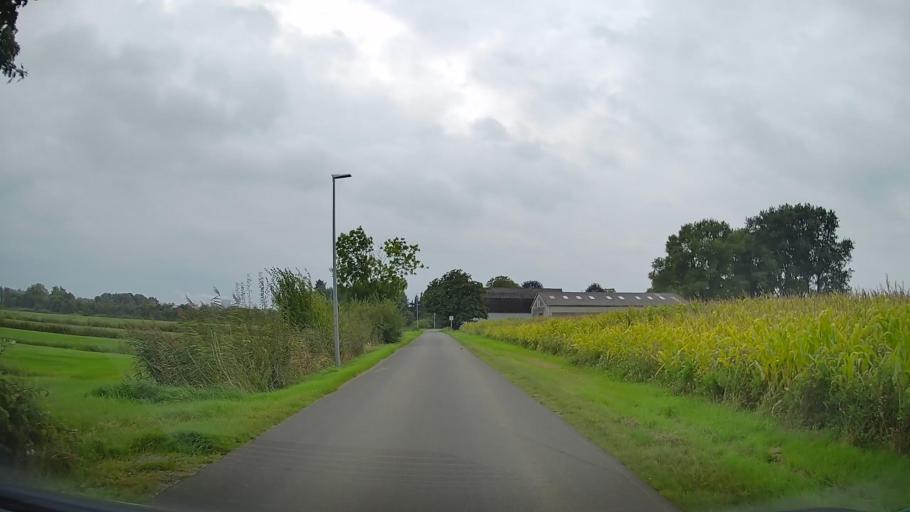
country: DE
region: Schleswig-Holstein
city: Kollmar
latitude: 53.6742
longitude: 9.4883
